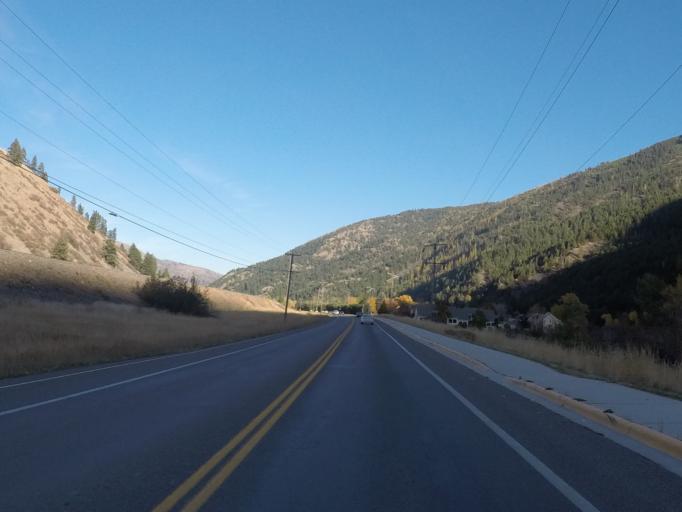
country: US
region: Montana
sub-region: Missoula County
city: East Missoula
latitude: 46.8629
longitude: -113.9643
